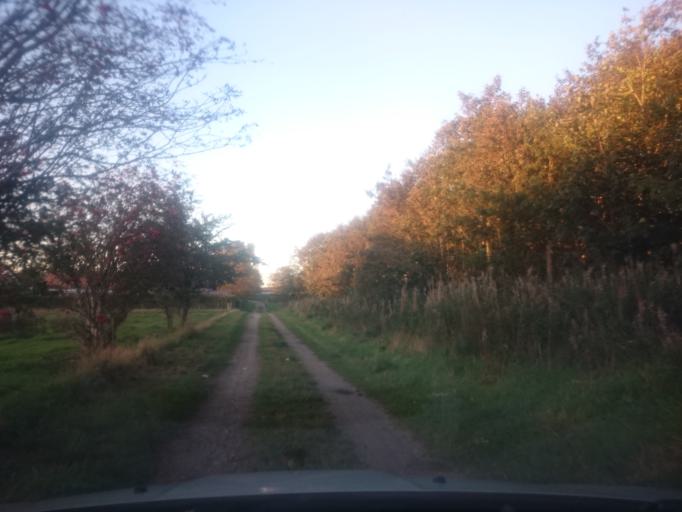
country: DK
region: South Denmark
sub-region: Billund Kommune
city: Billund
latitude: 55.7272
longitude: 9.0928
